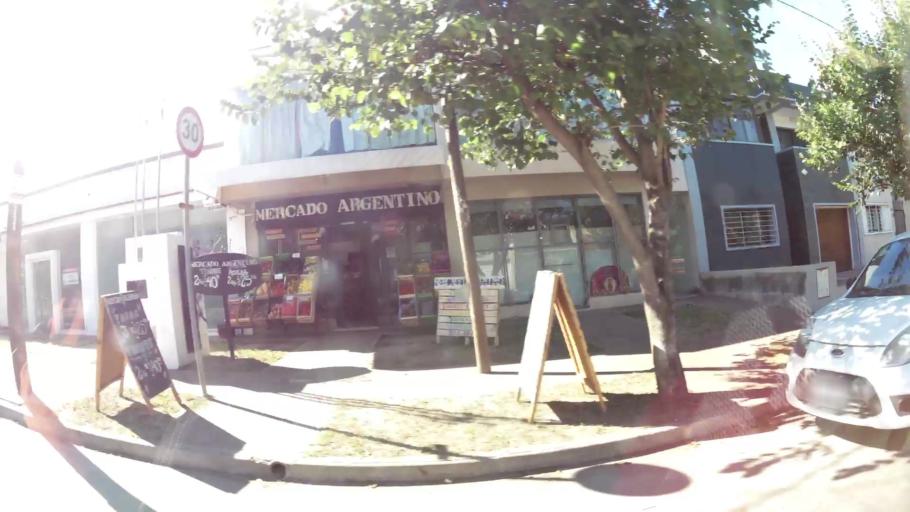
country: AR
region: Cordoba
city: Villa Allende
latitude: -31.3480
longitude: -64.2445
